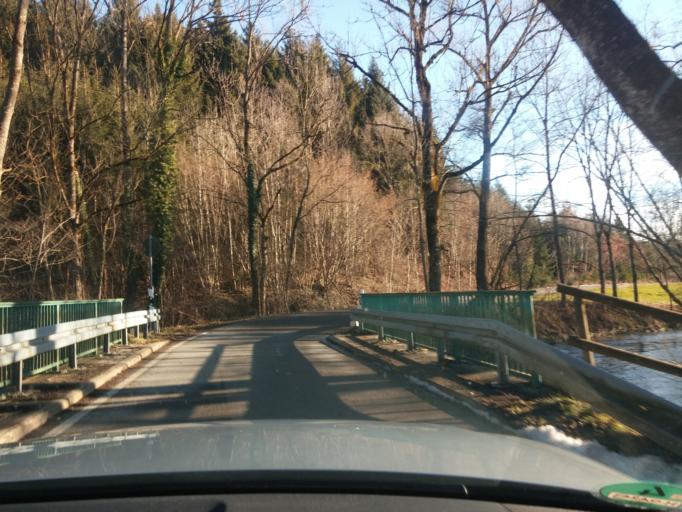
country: DE
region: Bavaria
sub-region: Swabia
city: Legau
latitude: 47.8576
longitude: 10.1045
